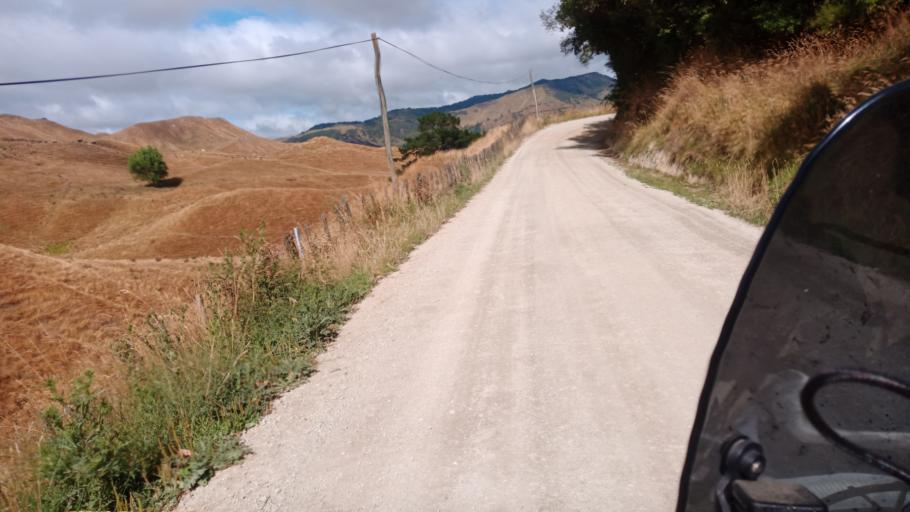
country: NZ
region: Hawke's Bay
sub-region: Wairoa District
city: Wairoa
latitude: -38.6073
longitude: 177.4572
